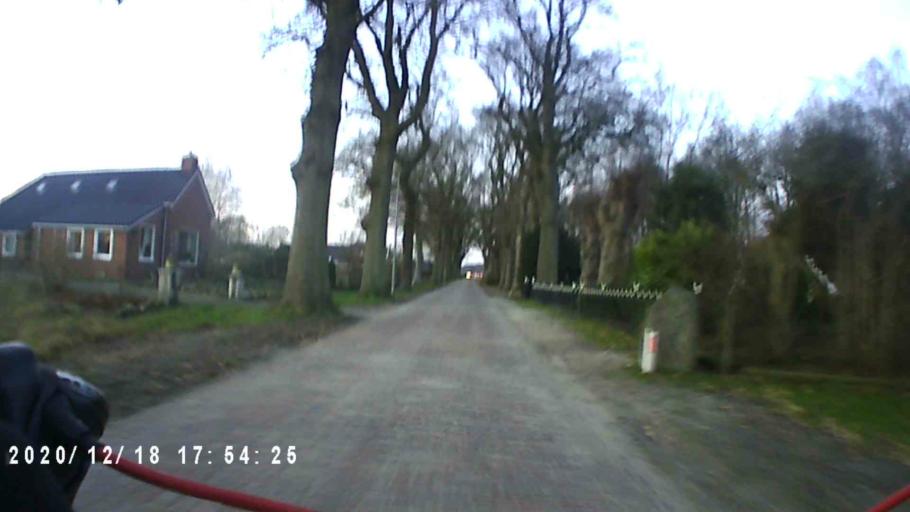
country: NL
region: Drenthe
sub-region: Gemeente Tynaarlo
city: Tynaarlo
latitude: 53.1231
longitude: 6.5980
